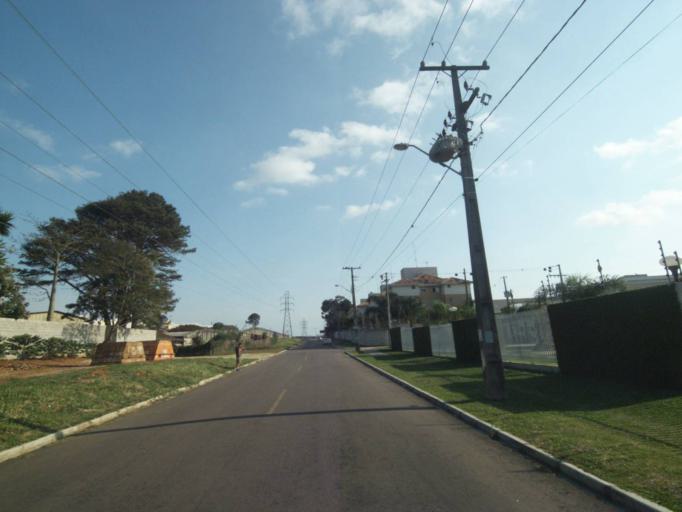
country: BR
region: Parana
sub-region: Curitiba
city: Curitiba
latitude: -25.4862
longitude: -49.3225
